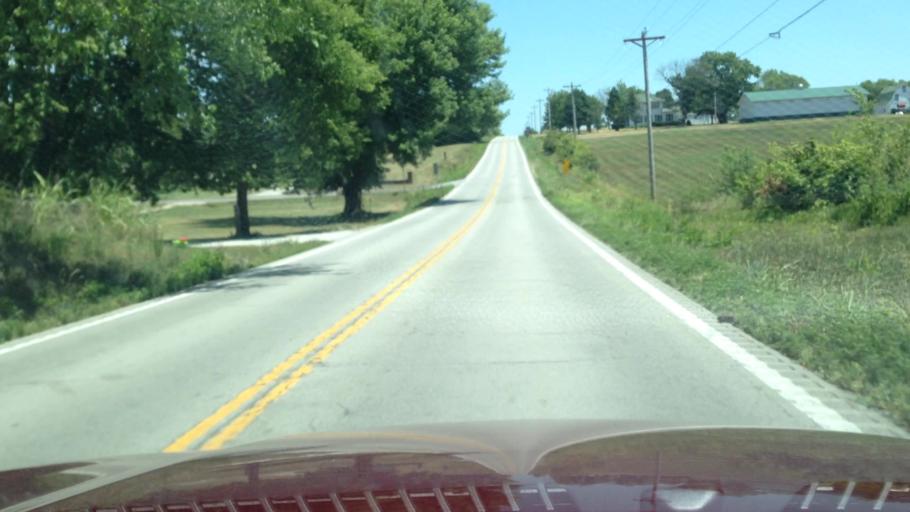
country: US
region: Missouri
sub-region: Clay County
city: Kearney
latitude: 39.3679
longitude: -94.4540
